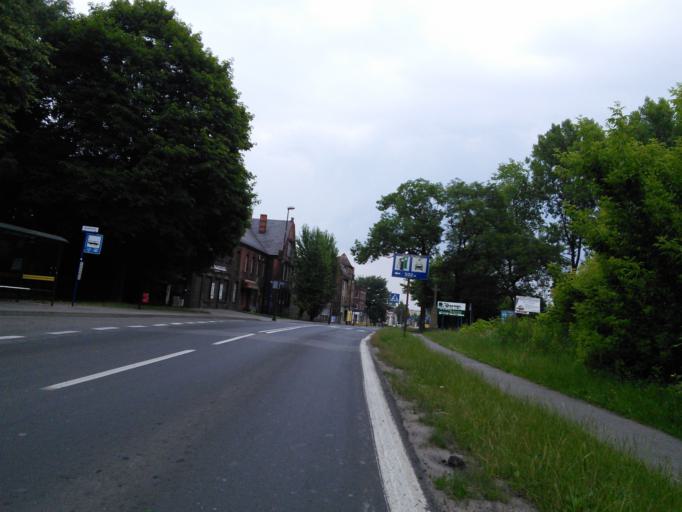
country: PL
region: Silesian Voivodeship
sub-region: Piekary Slaskie
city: Brzeziny Slaskie
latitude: 50.3699
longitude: 18.9703
